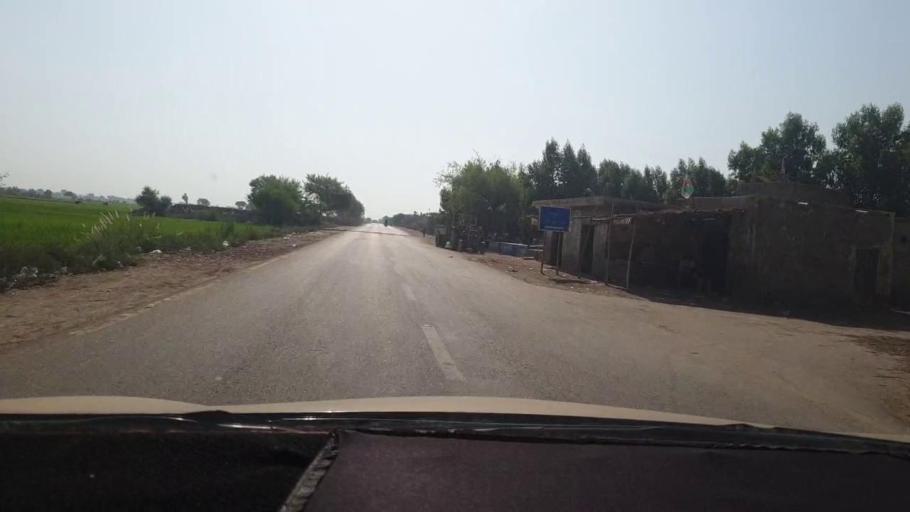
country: PK
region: Sindh
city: Miro Khan
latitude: 27.7334
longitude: 68.1184
